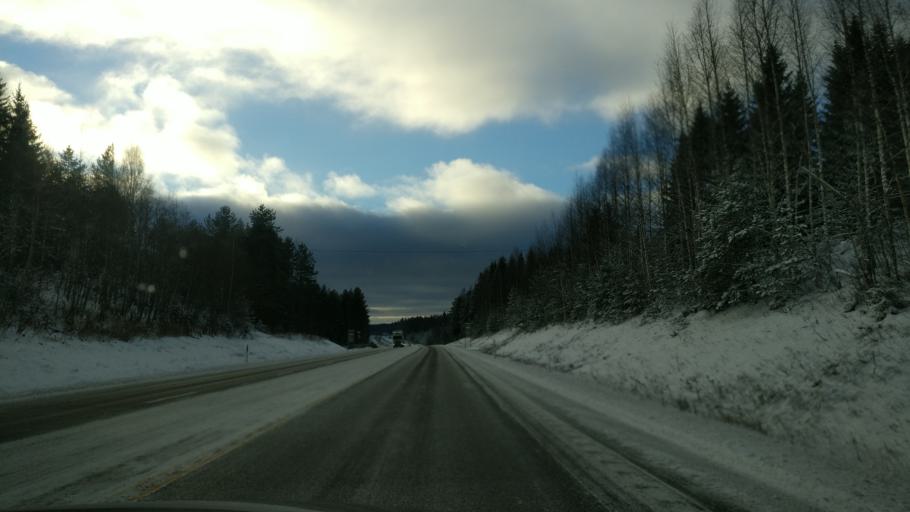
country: FI
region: Paijanne Tavastia
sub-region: Lahti
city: Heinola
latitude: 61.3446
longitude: 26.1996
